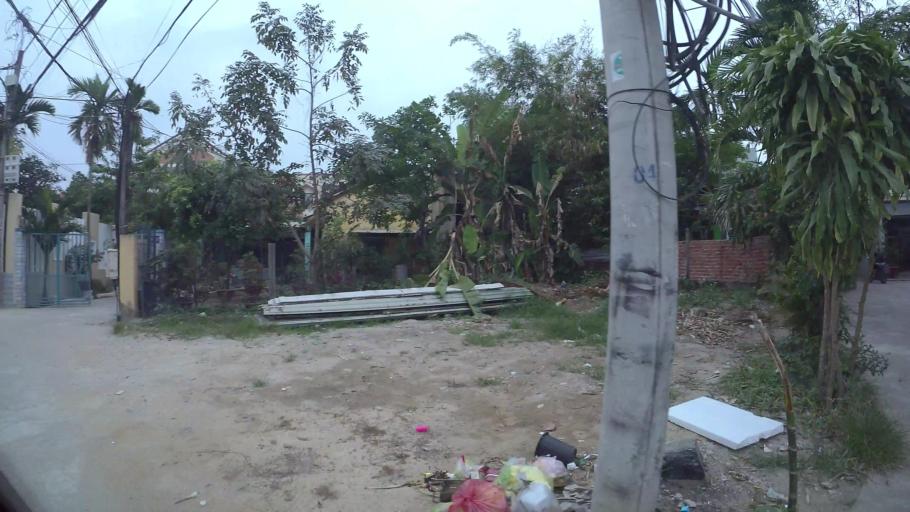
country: VN
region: Da Nang
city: Thanh Khe
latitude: 16.0458
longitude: 108.1805
